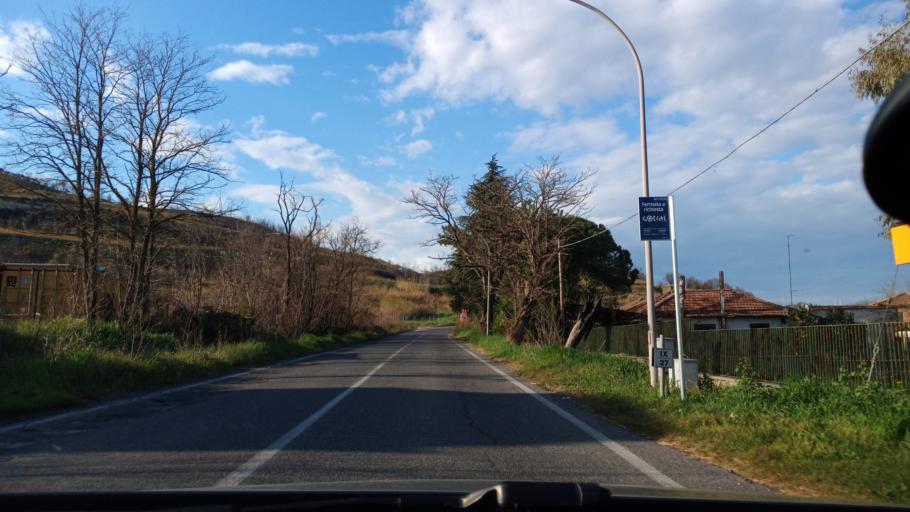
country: IT
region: Latium
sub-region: Citta metropolitana di Roma Capitale
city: Nazzano
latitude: 42.2016
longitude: 12.6051
